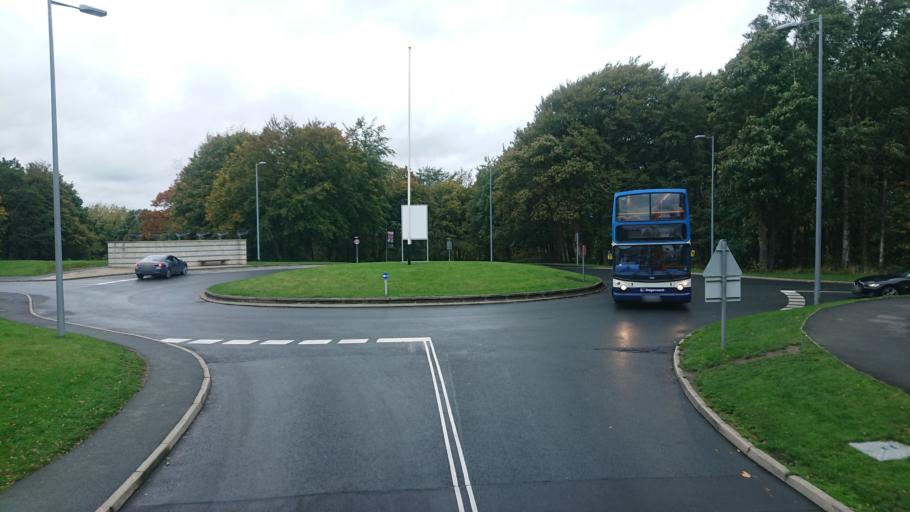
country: GB
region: England
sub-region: Lancashire
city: Galgate
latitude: 54.0102
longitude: -2.7879
